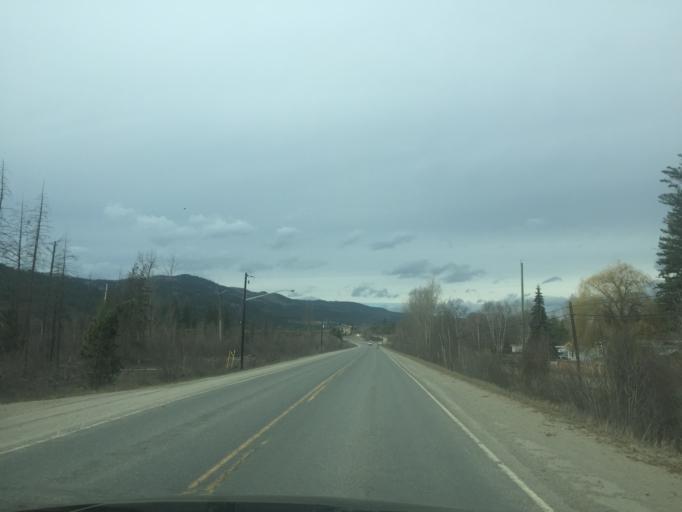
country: CA
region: British Columbia
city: Kamloops
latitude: 51.1788
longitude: -120.1343
